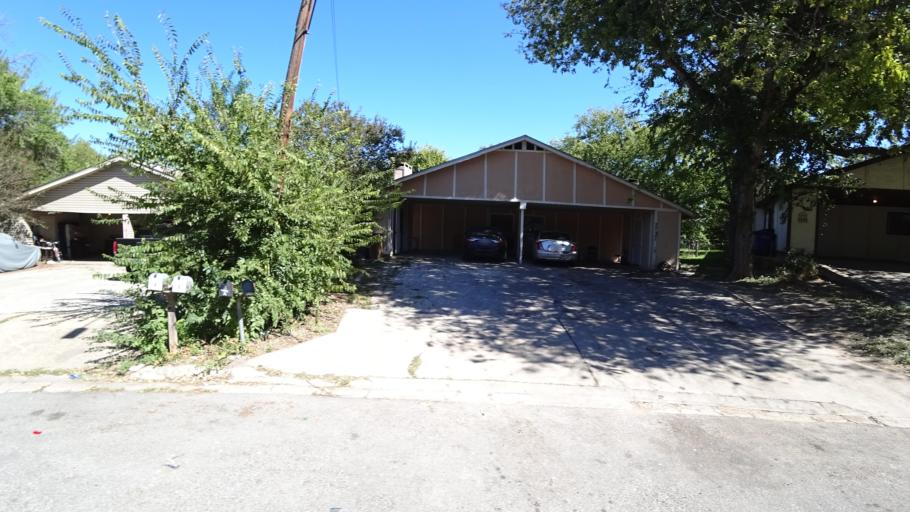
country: US
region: Texas
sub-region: Travis County
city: Austin
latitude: 30.2283
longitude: -97.7421
